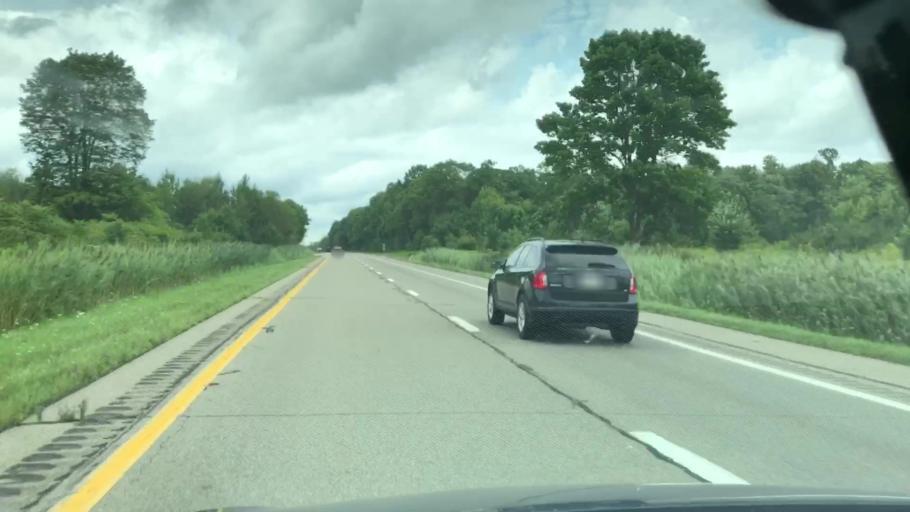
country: US
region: Pennsylvania
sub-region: Erie County
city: Edinboro
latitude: 41.8255
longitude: -80.1748
